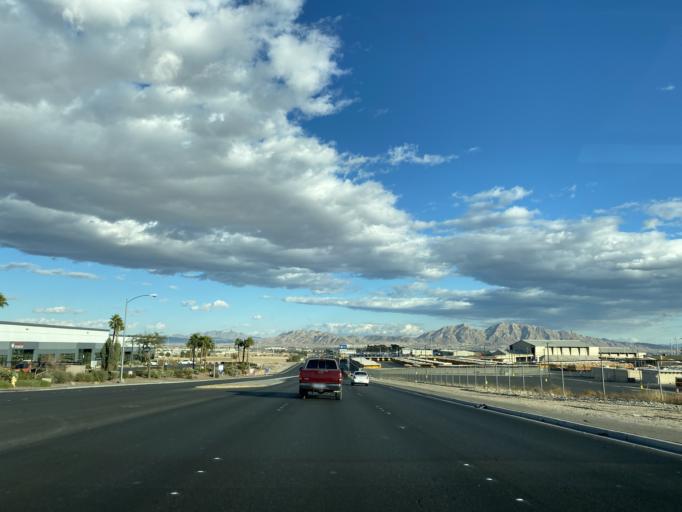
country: US
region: Nevada
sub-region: Clark County
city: North Las Vegas
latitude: 36.2178
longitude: -115.1502
